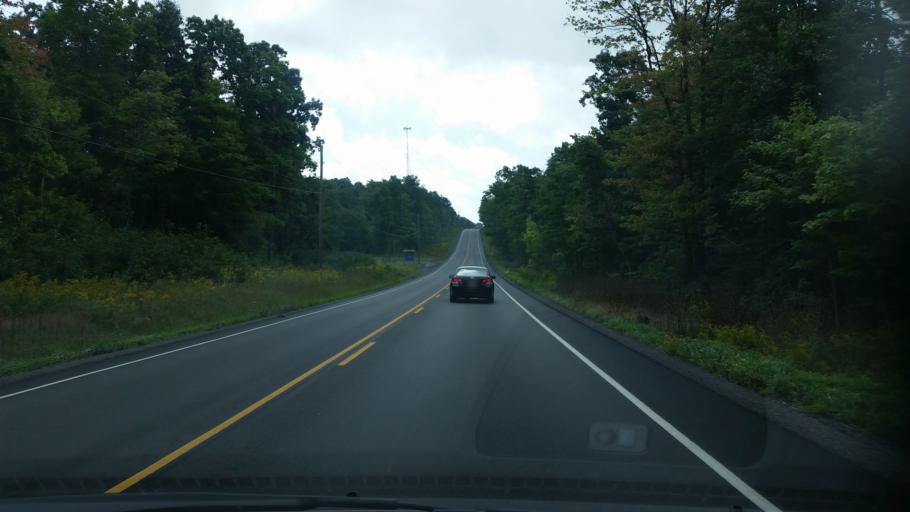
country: US
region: Pennsylvania
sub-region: Centre County
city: Philipsburg
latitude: 40.8635
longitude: -78.1686
